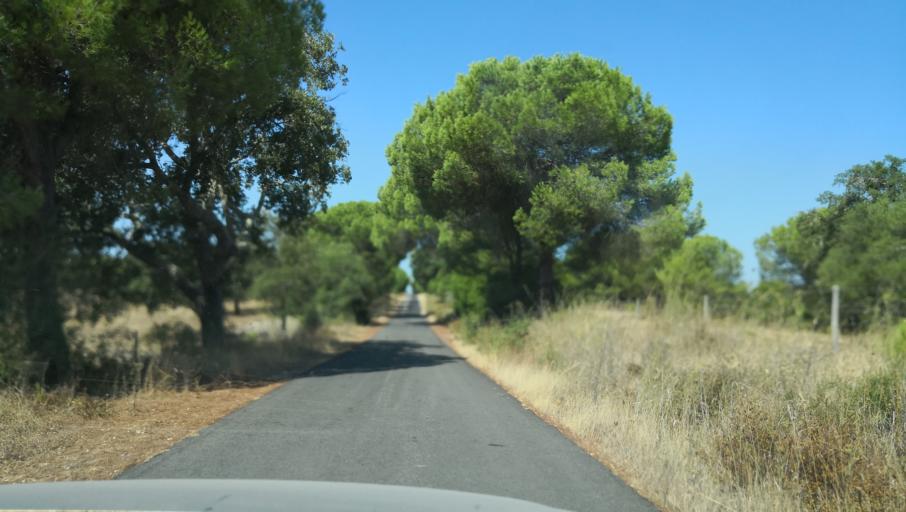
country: PT
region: Setubal
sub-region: Alcacer do Sal
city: Alcacer do Sal
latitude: 38.2558
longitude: -8.3021
